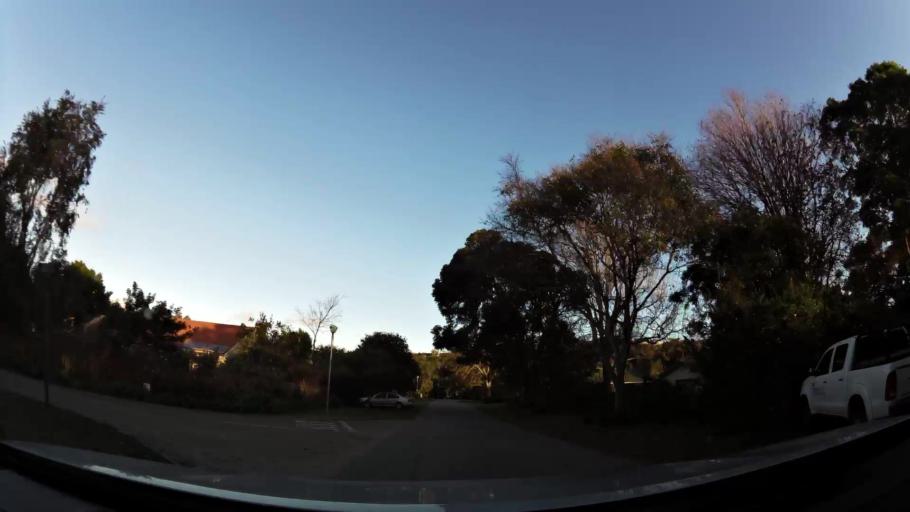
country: ZA
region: Western Cape
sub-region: Eden District Municipality
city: Knysna
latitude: -34.0191
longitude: 22.8044
